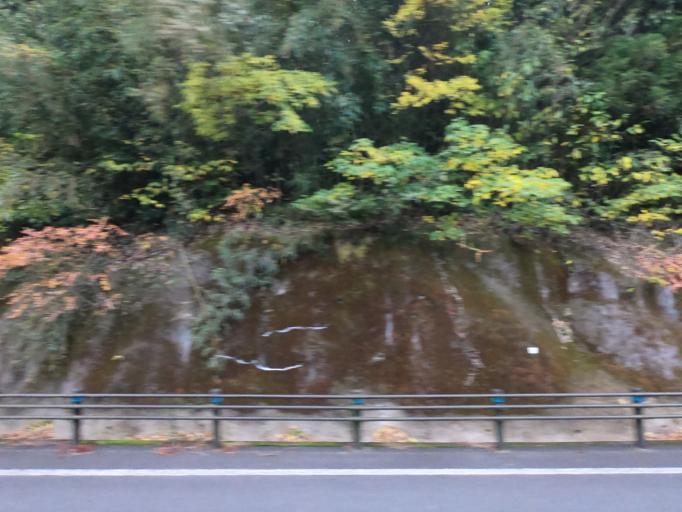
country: JP
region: Kumamoto
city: Minamata
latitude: 32.2596
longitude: 130.5099
